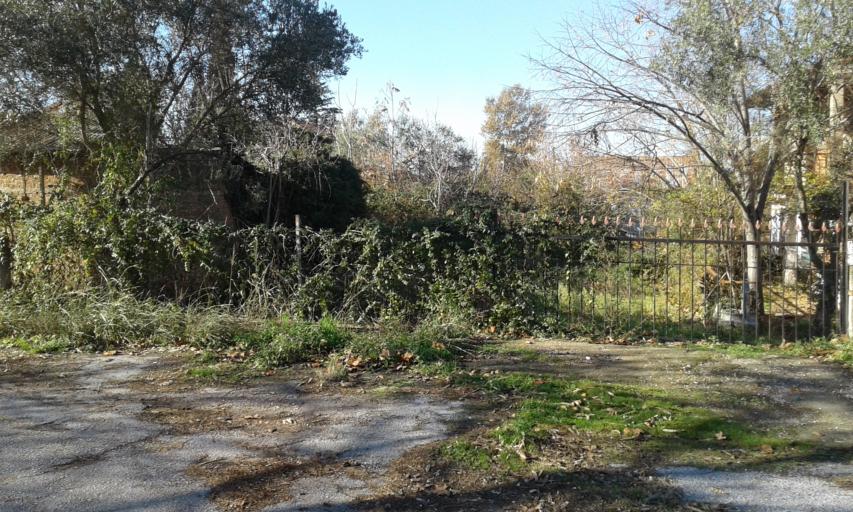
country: GR
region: Central Macedonia
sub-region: Nomos Thessalonikis
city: Gerakarou
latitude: 40.6374
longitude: 23.2471
